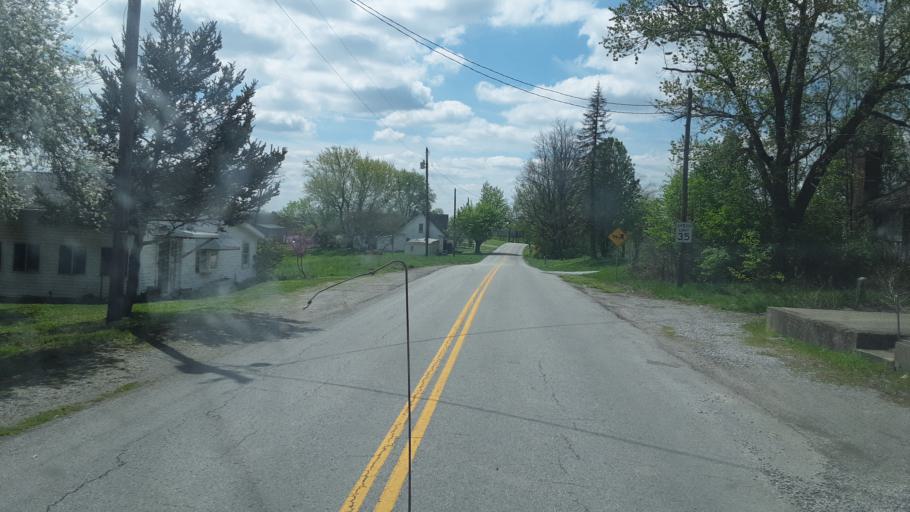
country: US
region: Kentucky
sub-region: Owen County
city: Owenton
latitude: 38.6370
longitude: -84.7766
